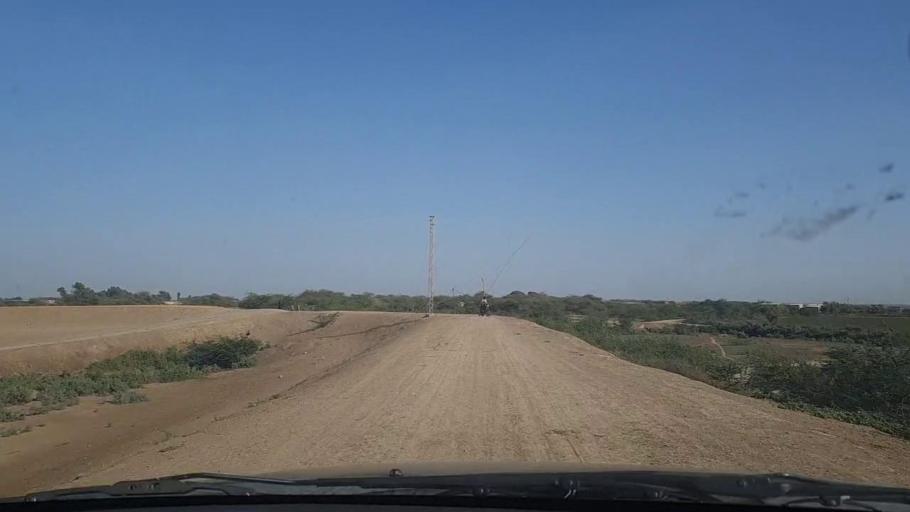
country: PK
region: Sindh
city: Chuhar Jamali
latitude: 24.3668
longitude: 67.7778
